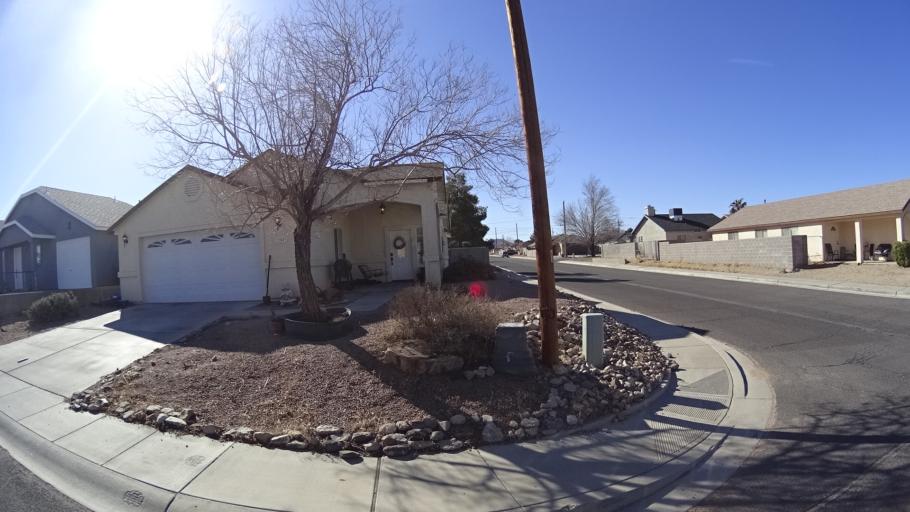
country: US
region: Arizona
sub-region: Mohave County
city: Kingman
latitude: 35.2014
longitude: -114.0158
